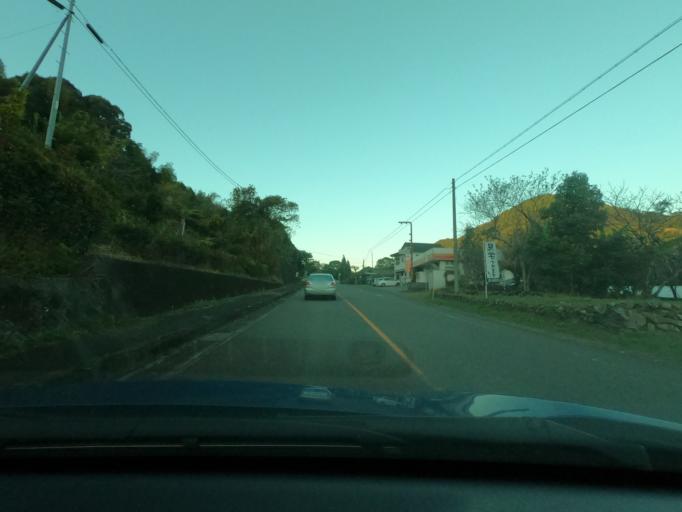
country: JP
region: Kagoshima
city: Satsumasendai
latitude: 31.8007
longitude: 130.4797
